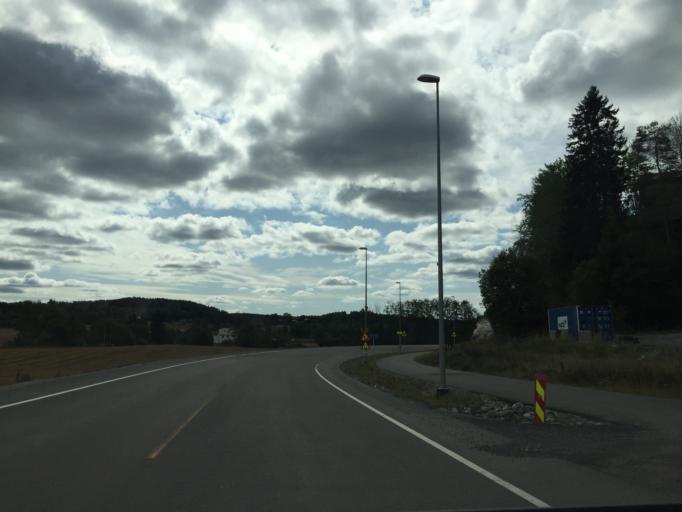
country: NO
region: Ostfold
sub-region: Hobol
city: Elvestad
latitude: 59.6262
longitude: 10.9543
